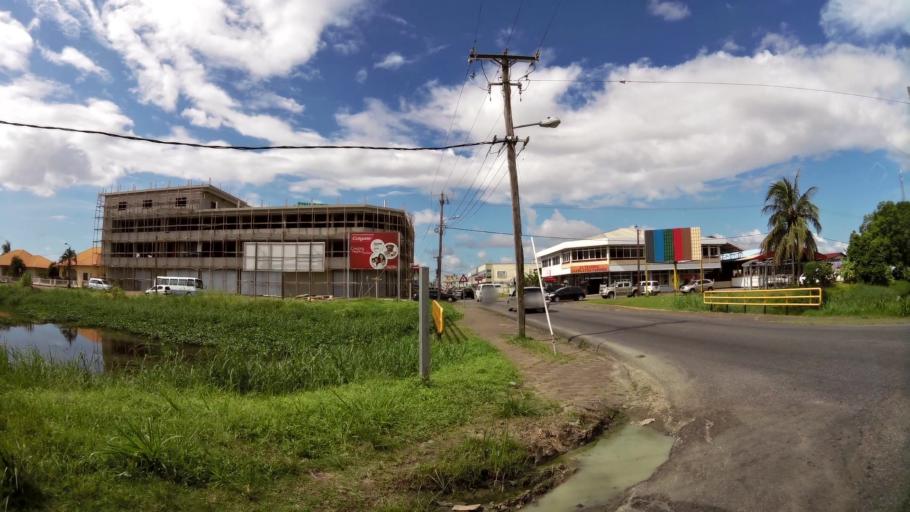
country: SR
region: Paramaribo
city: Paramaribo
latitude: 5.8472
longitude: -55.1410
